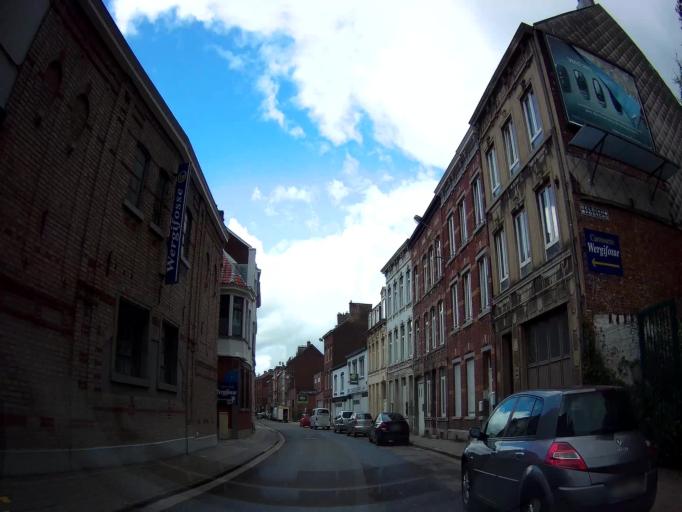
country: BE
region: Wallonia
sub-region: Province de Liege
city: Verviers
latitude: 50.5876
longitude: 5.8740
